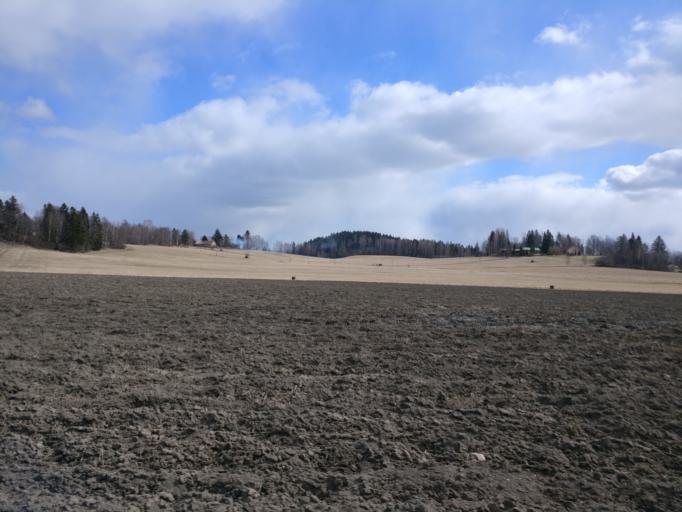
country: FI
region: Uusimaa
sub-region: Helsinki
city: Karjalohja
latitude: 60.2436
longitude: 23.7383
